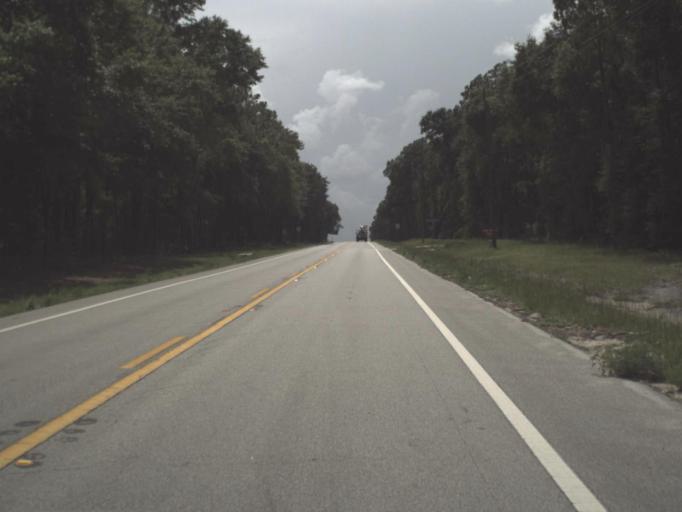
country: US
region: Florida
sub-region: Madison County
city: Madison
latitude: 30.4710
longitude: -83.3665
